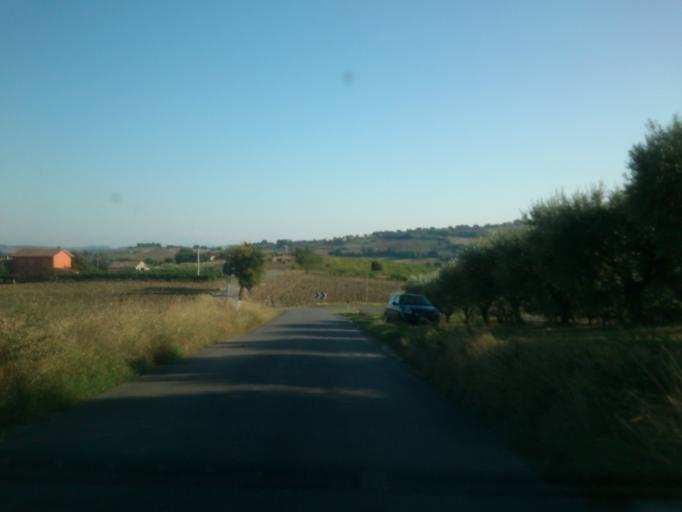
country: IT
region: The Marches
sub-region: Provincia di Pesaro e Urbino
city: Lucrezia
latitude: 43.7869
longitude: 12.9101
